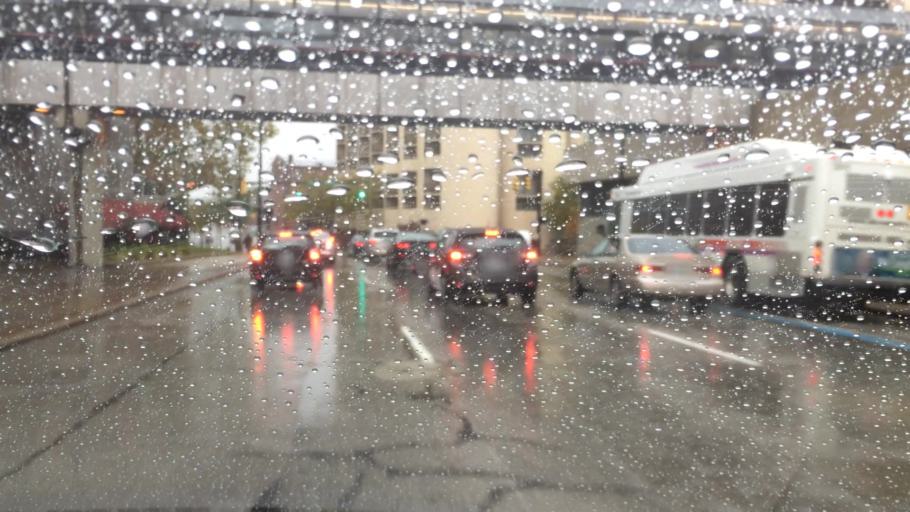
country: US
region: Ohio
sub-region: Summit County
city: Akron
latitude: 41.0799
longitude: -81.5166
